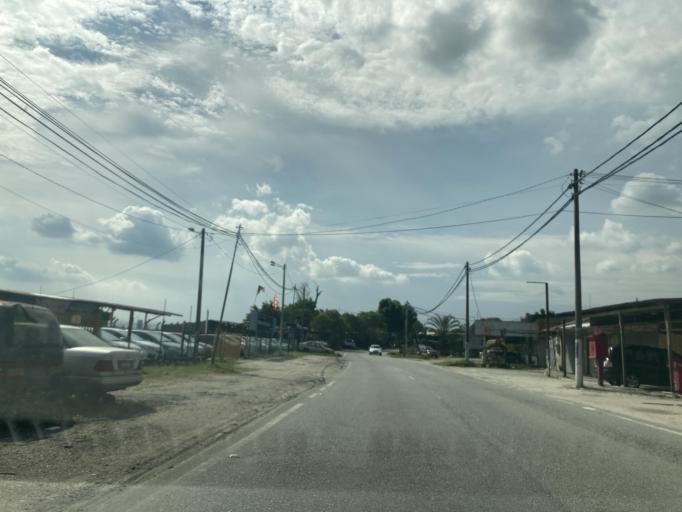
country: MY
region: Selangor
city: Kampung Baru Subang
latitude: 3.1422
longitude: 101.5459
